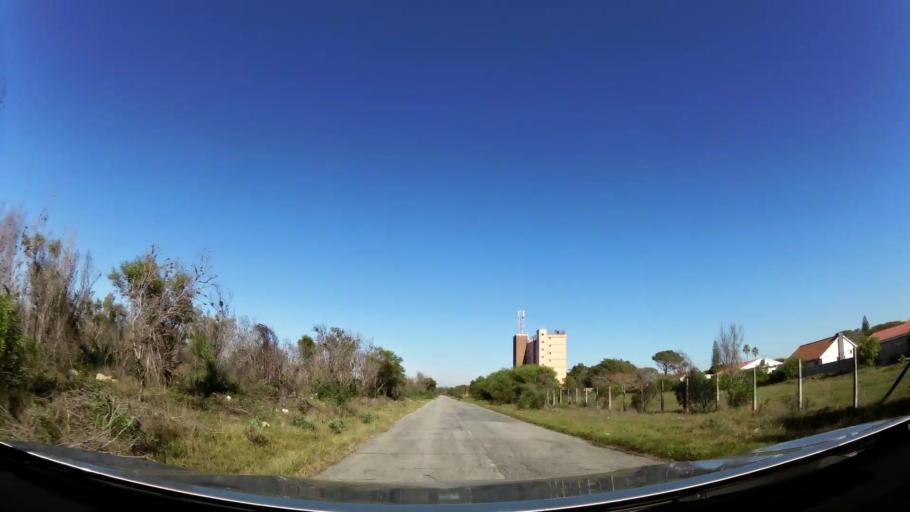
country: ZA
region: Eastern Cape
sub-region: Nelson Mandela Bay Metropolitan Municipality
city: Port Elizabeth
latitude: -33.9886
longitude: 25.6311
